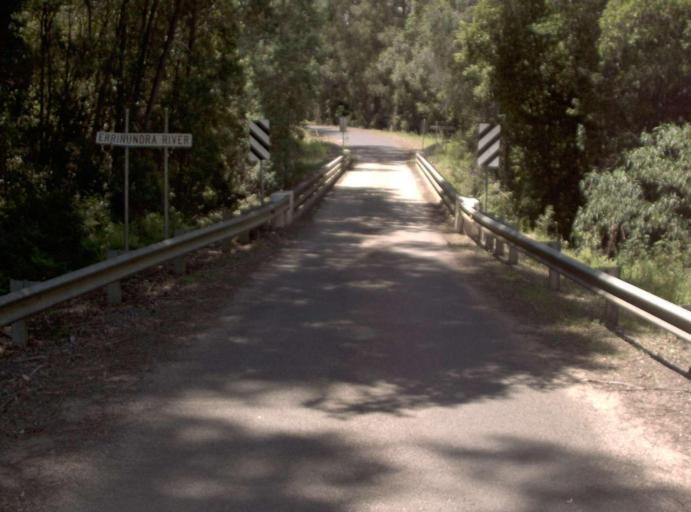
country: AU
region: New South Wales
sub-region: Bombala
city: Bombala
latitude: -37.4743
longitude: 148.9260
